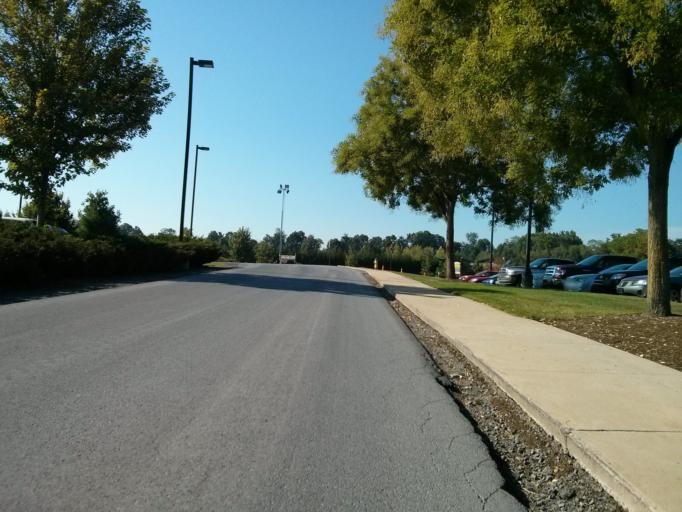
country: US
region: Pennsylvania
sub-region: Centre County
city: State College
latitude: 40.8077
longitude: -77.8679
